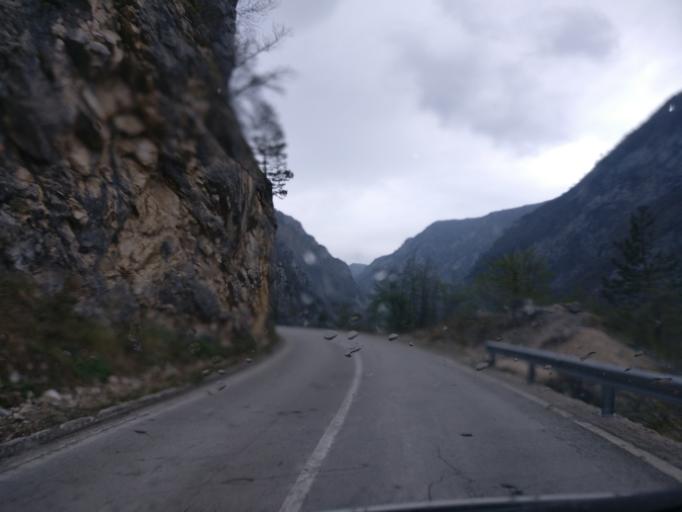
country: ME
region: Opstina Pluzine
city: Pluzine
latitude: 43.2089
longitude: 18.8589
